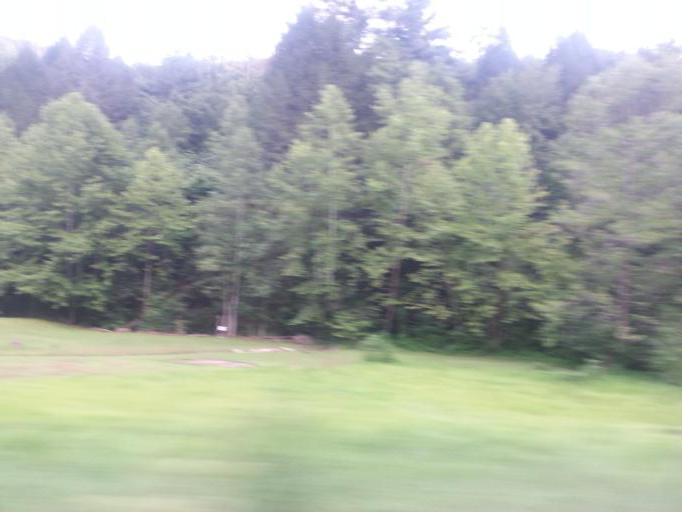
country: US
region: Tennessee
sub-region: Anderson County
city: Clinton
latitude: 36.1314
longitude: -84.2193
